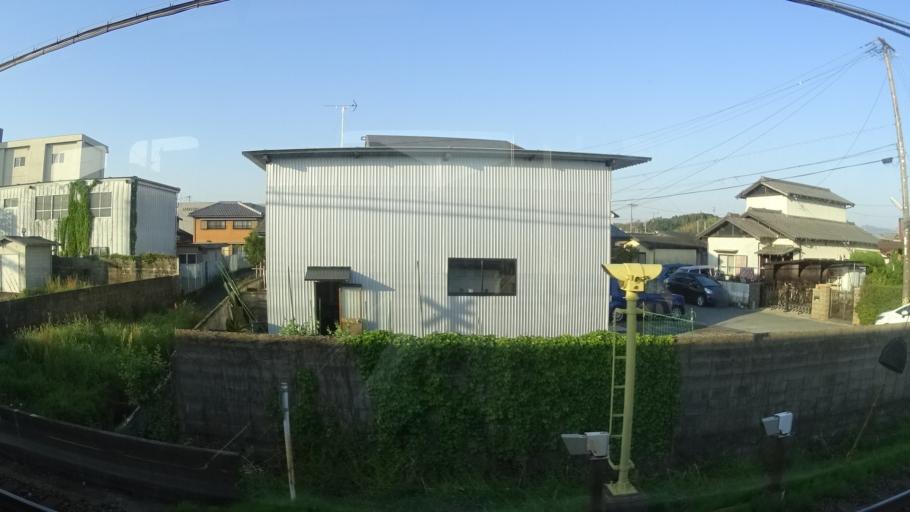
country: JP
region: Mie
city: Ise
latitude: 34.5496
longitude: 136.5811
